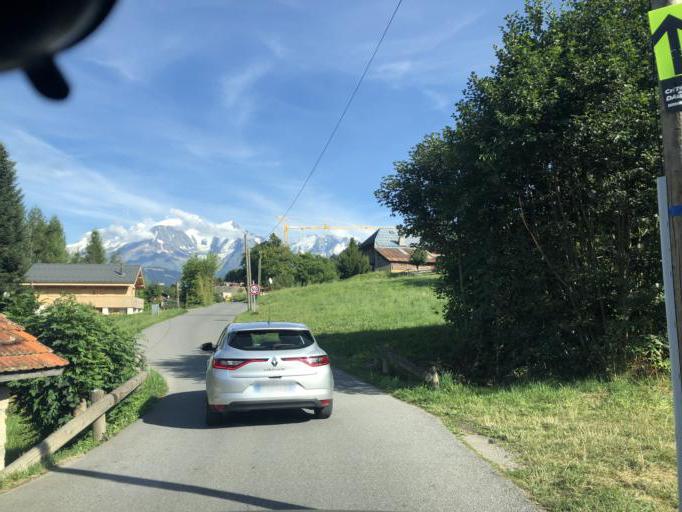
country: FR
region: Rhone-Alpes
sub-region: Departement de la Haute-Savoie
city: Cordon
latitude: 45.9144
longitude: 6.6138
